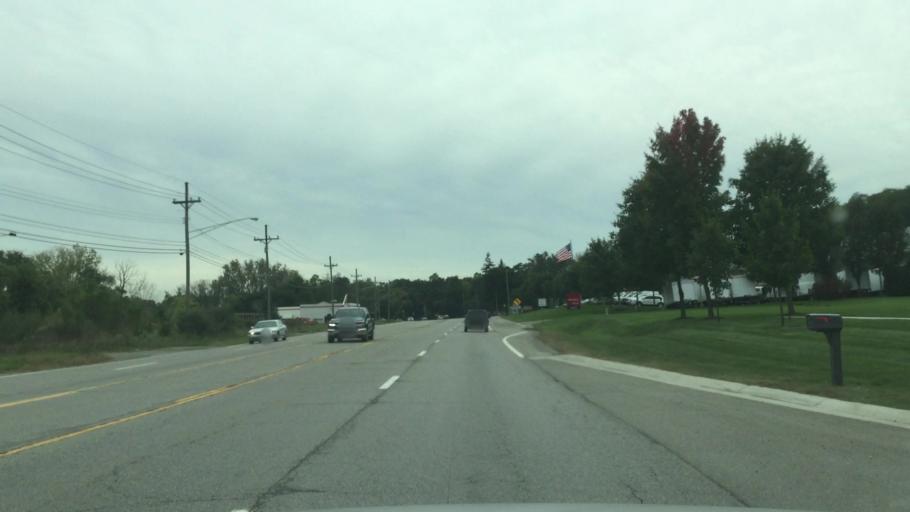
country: US
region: Michigan
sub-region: Oakland County
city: Clarkston
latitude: 42.7554
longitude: -83.4804
